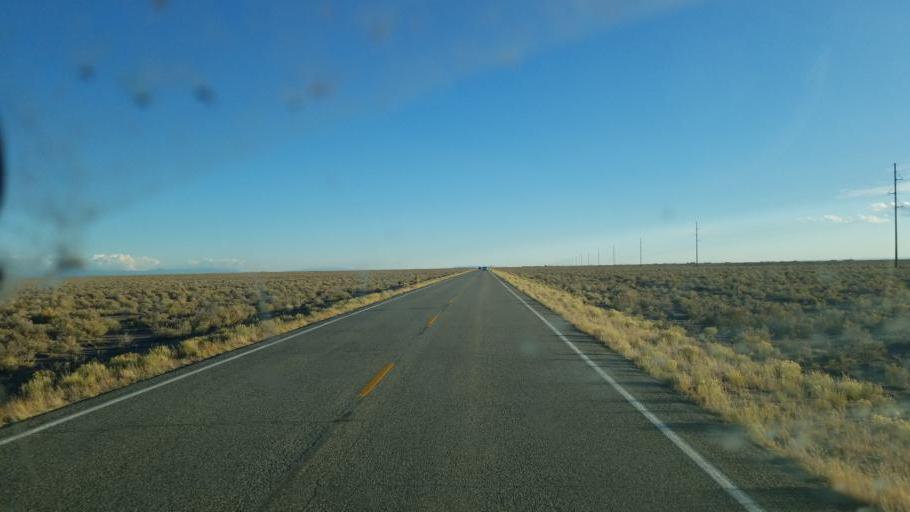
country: US
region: Colorado
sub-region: Saguache County
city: Center
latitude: 37.8436
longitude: -105.8912
